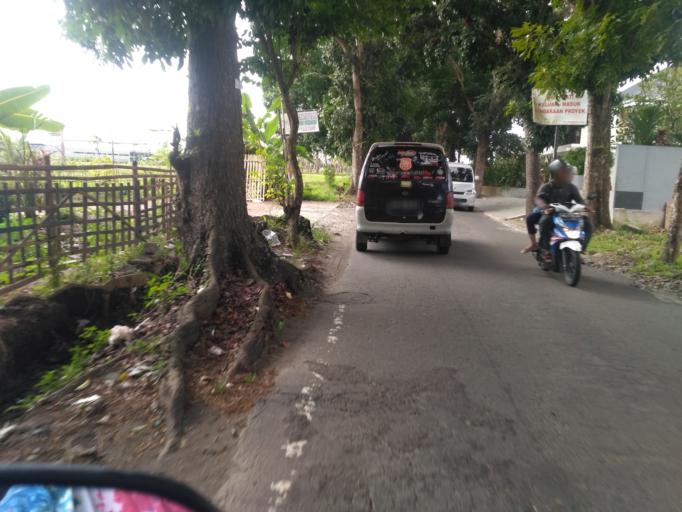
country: ID
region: Daerah Istimewa Yogyakarta
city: Melati
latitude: -7.7350
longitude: 110.3532
